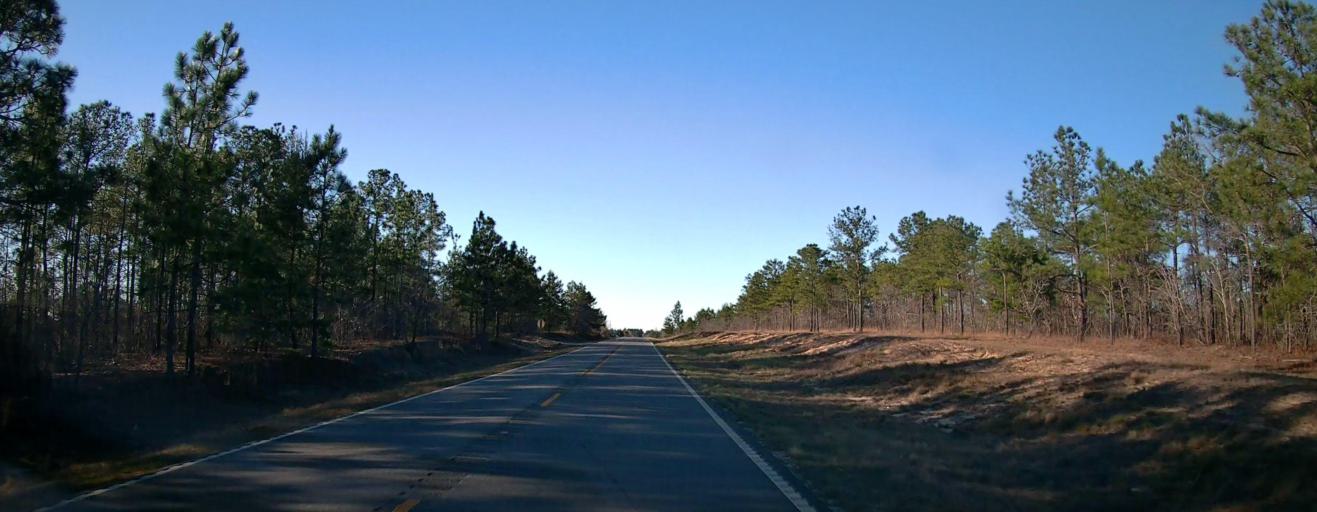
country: US
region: Georgia
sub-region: Talbot County
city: Talbotton
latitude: 32.5790
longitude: -84.4451
